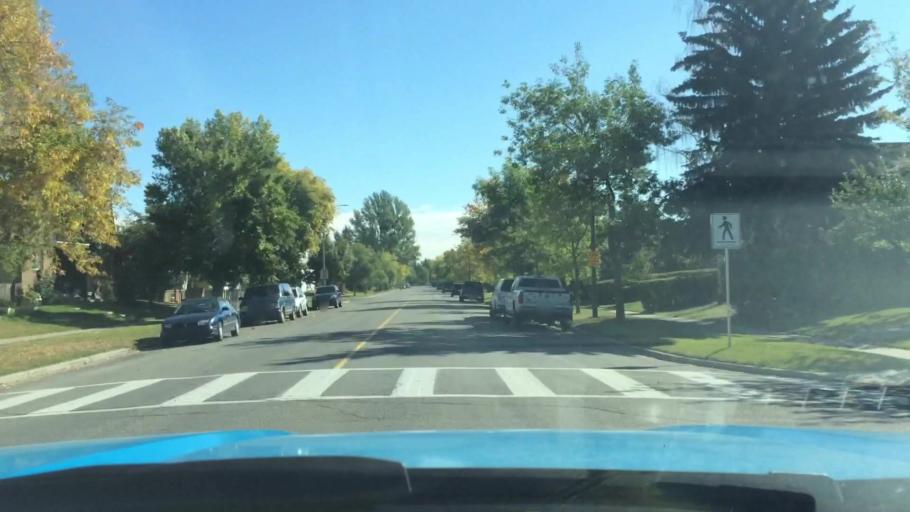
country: CA
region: Alberta
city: Calgary
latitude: 51.1178
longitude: -114.0600
